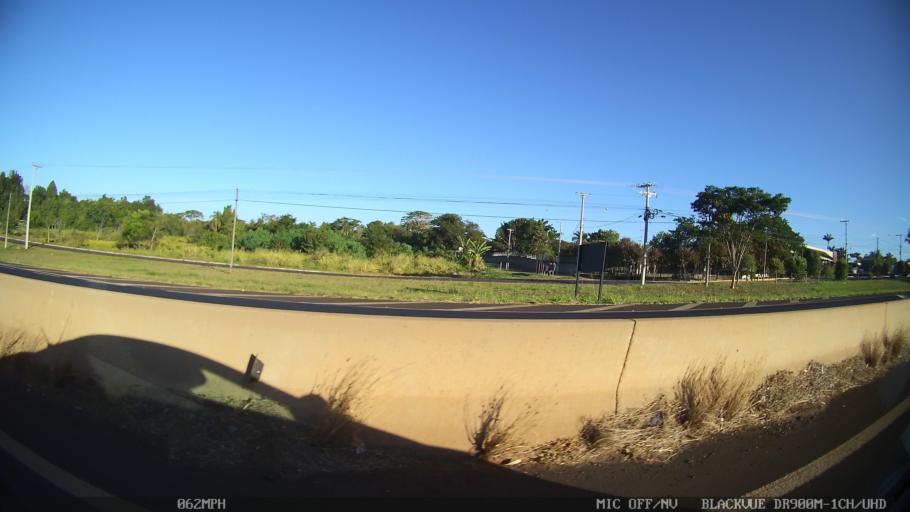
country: BR
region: Sao Paulo
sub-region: Guapiacu
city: Guapiacu
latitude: -20.7844
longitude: -49.2715
